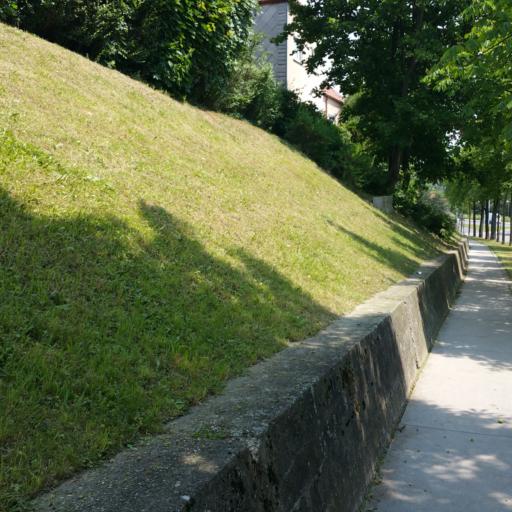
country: AT
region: Vienna
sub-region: Wien Stadt
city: Vienna
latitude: 48.2066
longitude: 16.2873
